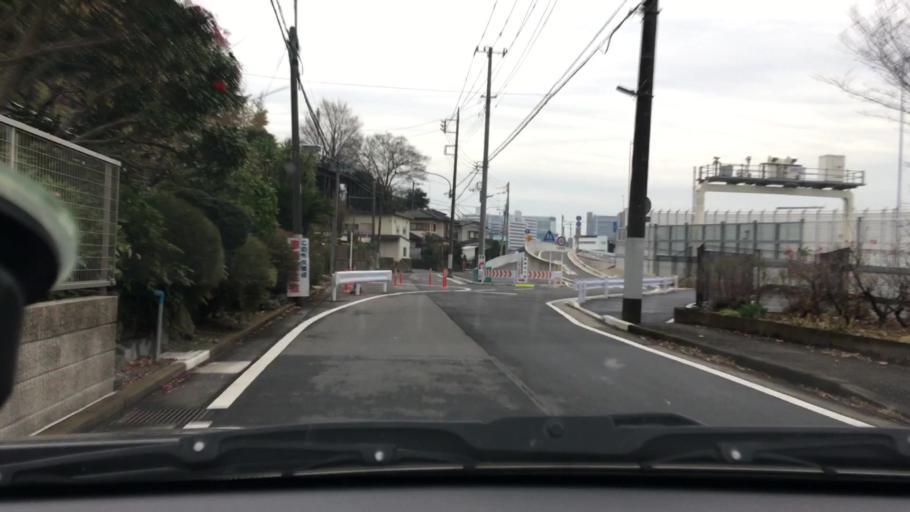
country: JP
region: Kanagawa
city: Yokohama
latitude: 35.5169
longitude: 139.6065
